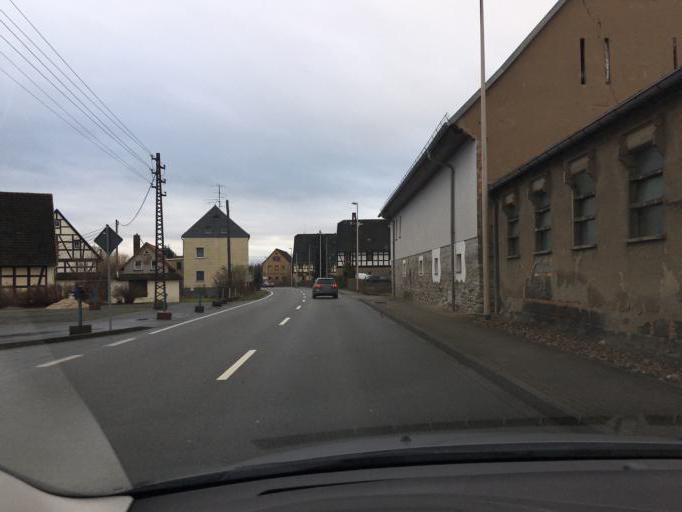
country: DE
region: Saxony
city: Waldenburg
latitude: 50.8666
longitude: 12.5851
